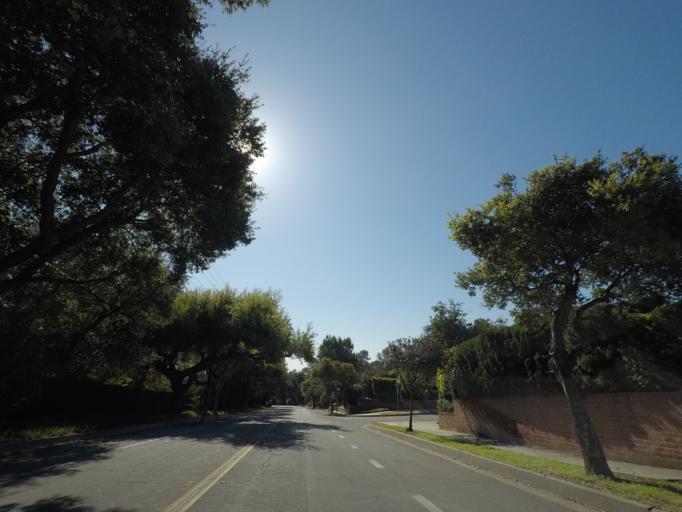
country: US
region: California
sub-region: Los Angeles County
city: La Canada Flintridge
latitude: 34.1722
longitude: -118.1836
